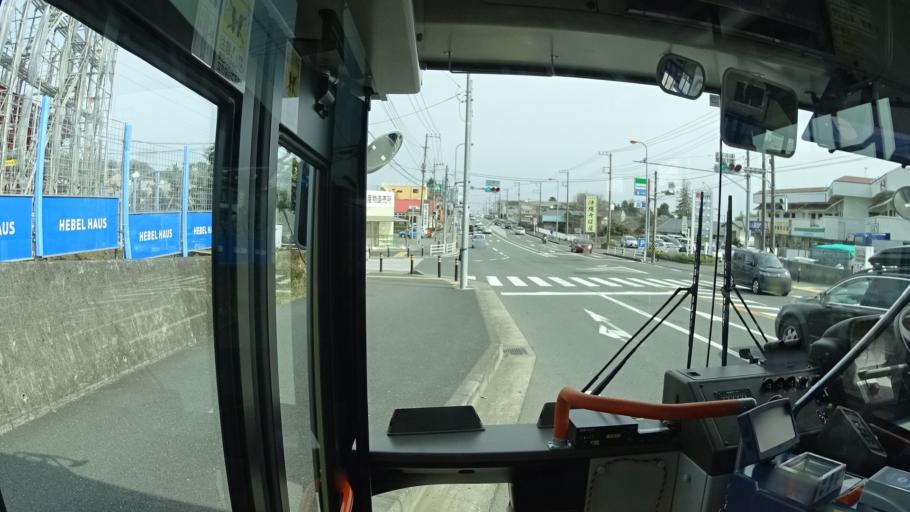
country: JP
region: Kanagawa
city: Atsugi
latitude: 35.4931
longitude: 139.3166
